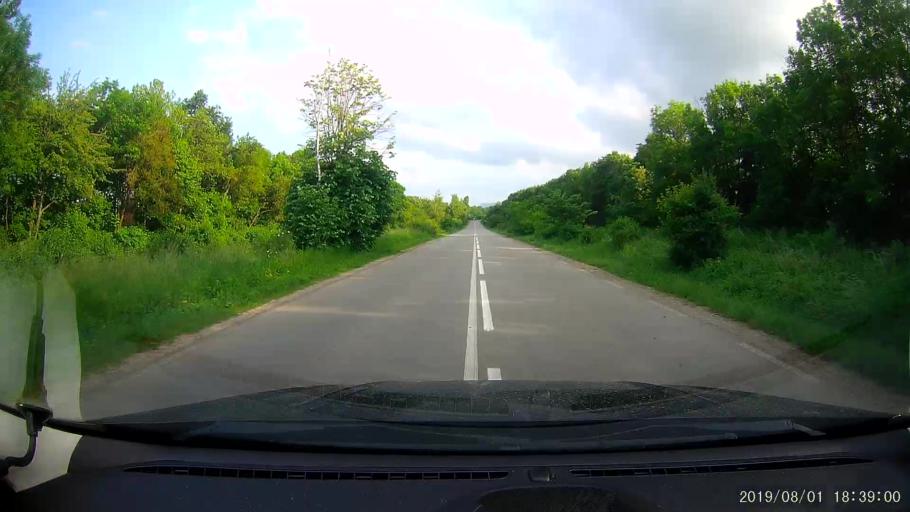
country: BG
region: Shumen
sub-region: Obshtina Khitrino
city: Gara Khitrino
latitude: 43.3946
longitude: 26.9172
